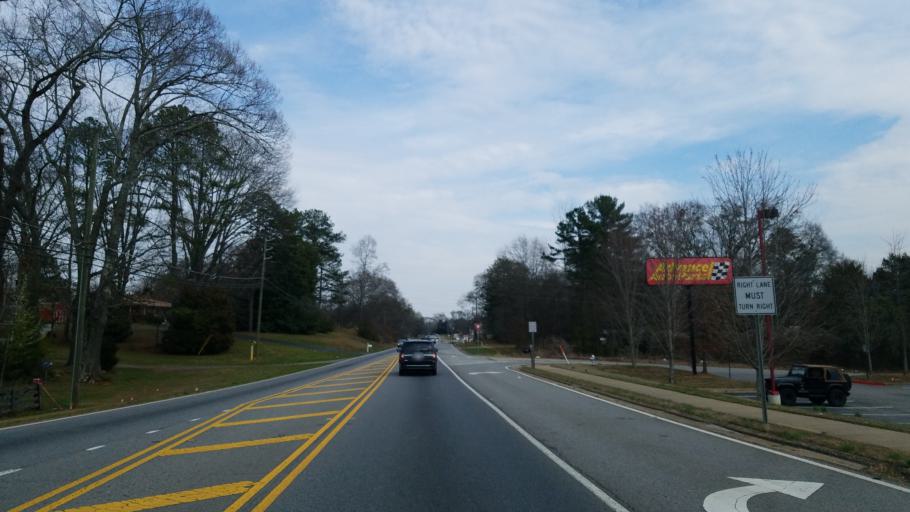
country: US
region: Georgia
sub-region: Cherokee County
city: Ball Ground
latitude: 34.2545
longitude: -84.3569
